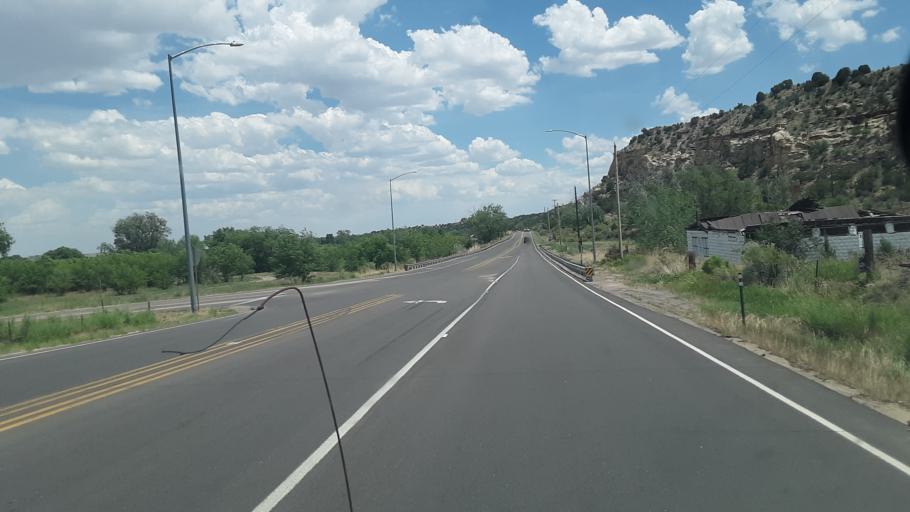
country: US
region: Colorado
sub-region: Fremont County
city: Lincoln Park
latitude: 38.4137
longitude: -105.1778
